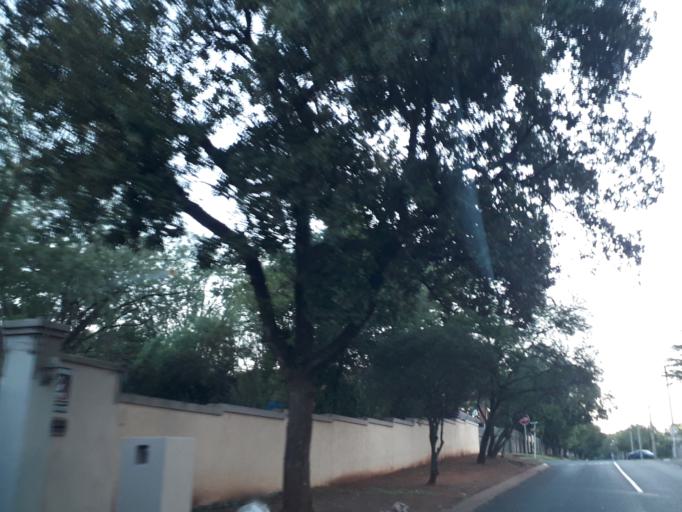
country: ZA
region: Gauteng
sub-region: City of Johannesburg Metropolitan Municipality
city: Roodepoort
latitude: -26.1363
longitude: 27.9388
